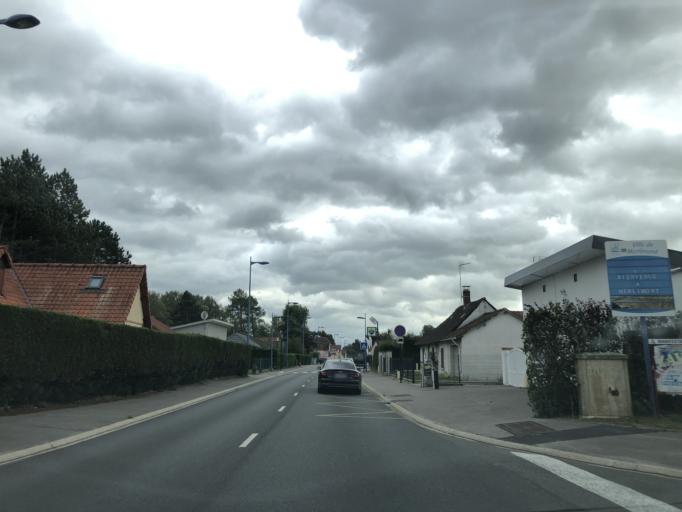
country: FR
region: Nord-Pas-de-Calais
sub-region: Departement du Pas-de-Calais
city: Merlimont
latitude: 50.4661
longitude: 1.6149
